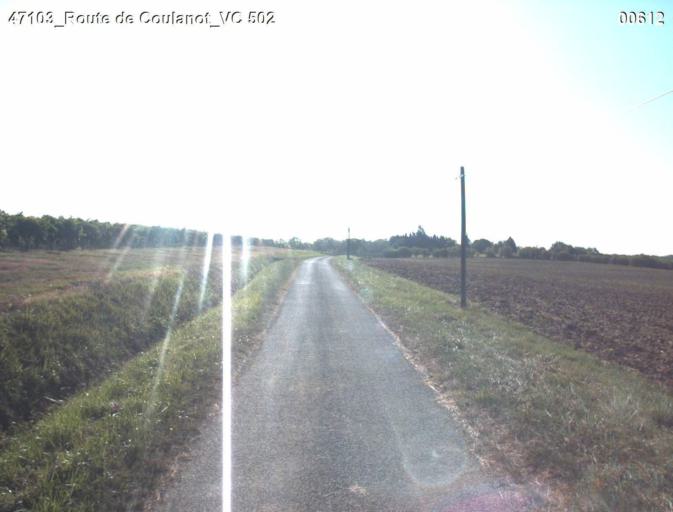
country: FR
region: Aquitaine
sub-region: Departement du Lot-et-Garonne
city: Nerac
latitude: 44.0740
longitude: 0.3361
